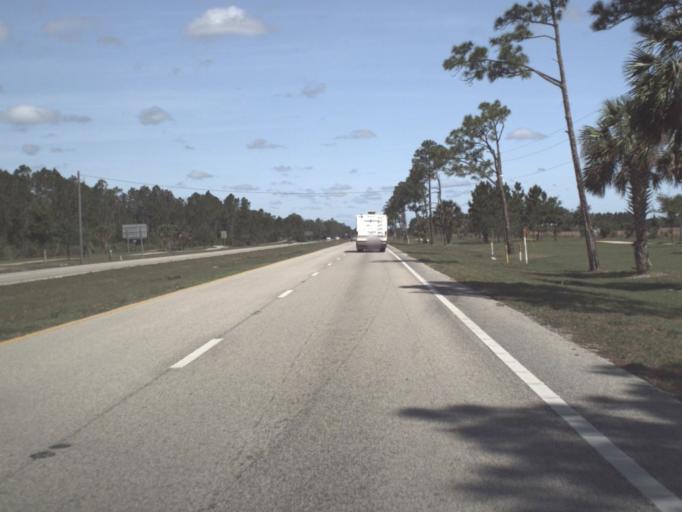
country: US
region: Florida
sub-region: Flagler County
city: Palm Coast
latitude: 29.5642
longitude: -81.2704
